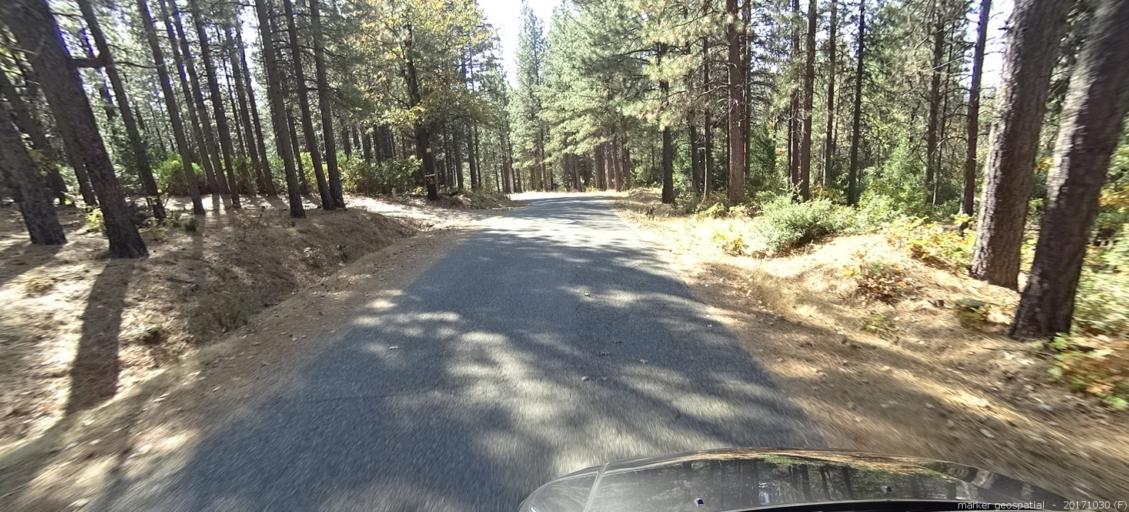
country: US
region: California
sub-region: Shasta County
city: Shingletown
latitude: 40.5922
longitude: -121.8622
